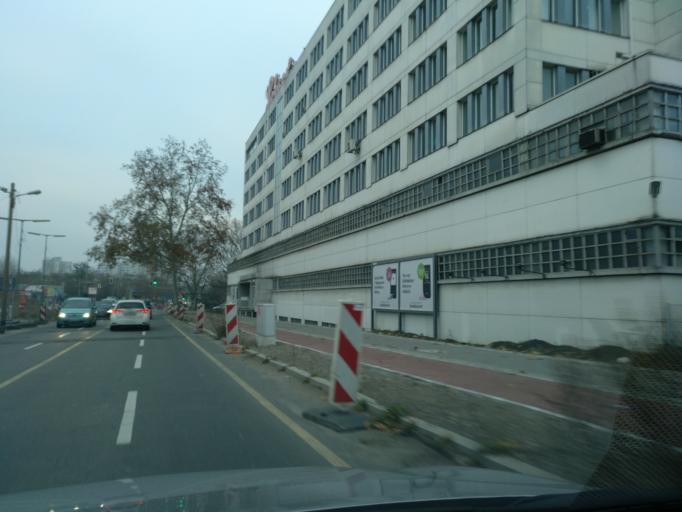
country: DE
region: Berlin
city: Plaenterwald
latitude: 52.4672
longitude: 13.4595
